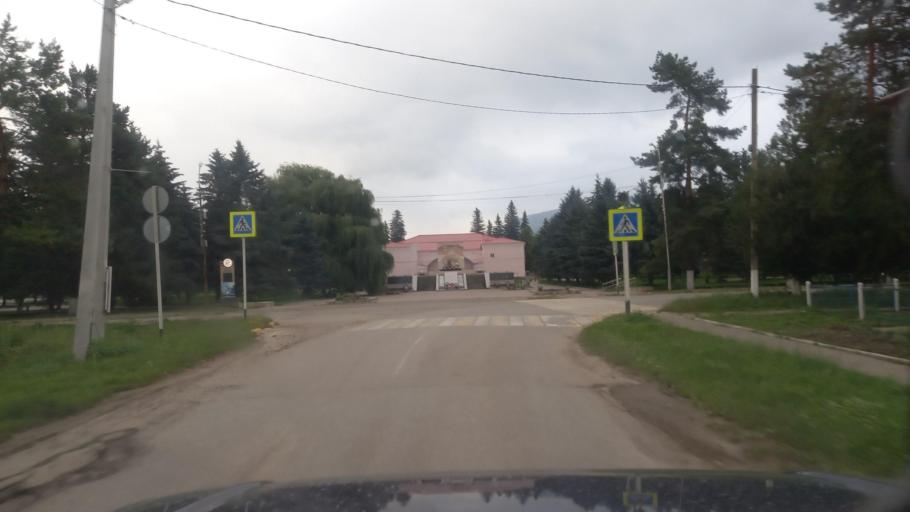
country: RU
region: Karachayevo-Cherkesiya
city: Pregradnaya
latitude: 43.9509
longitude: 41.1902
